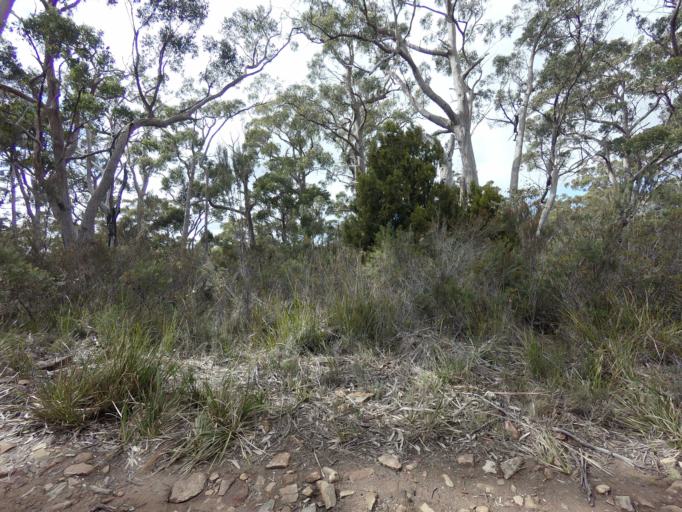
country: AU
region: Tasmania
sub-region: Huon Valley
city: Geeveston
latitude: -43.4793
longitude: 146.9341
